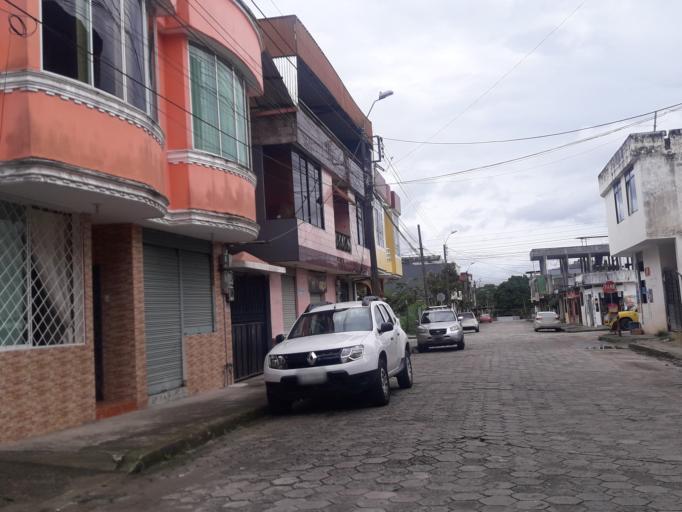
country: EC
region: Napo
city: Tena
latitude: -0.9971
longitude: -77.8098
